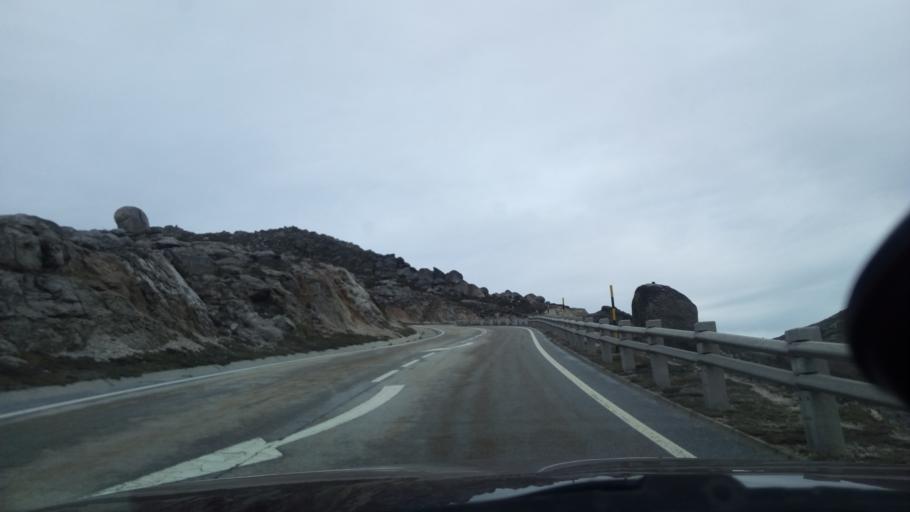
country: PT
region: Guarda
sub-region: Seia
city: Seia
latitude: 40.3528
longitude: -7.6834
